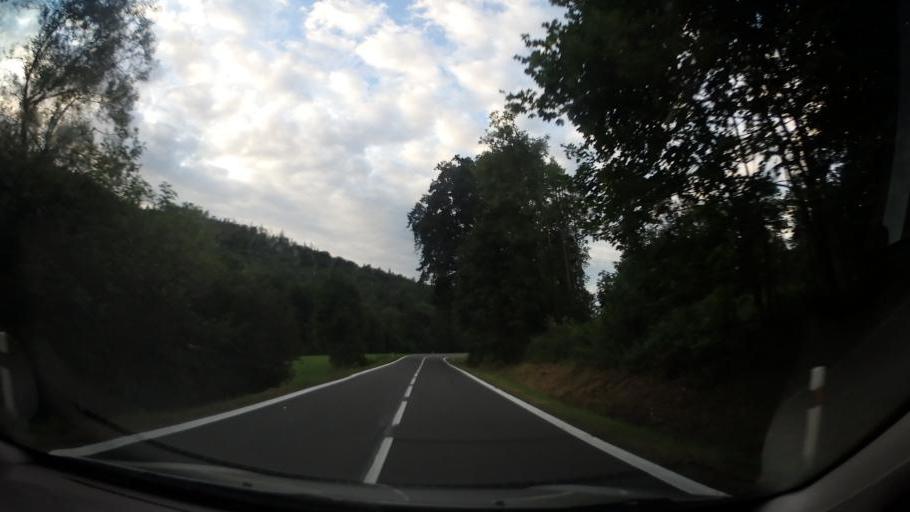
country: CZ
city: Horni Mesto
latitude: 49.8570
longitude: 17.2269
